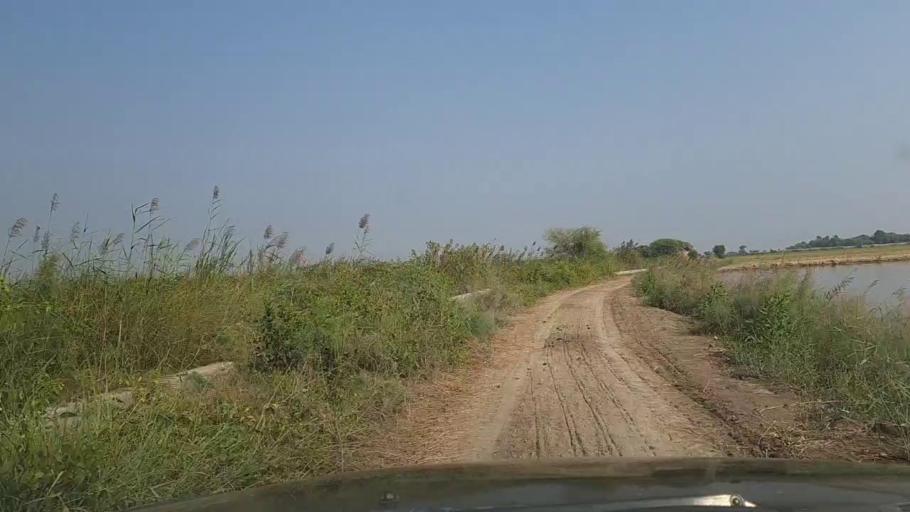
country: PK
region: Sindh
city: Mirpur Batoro
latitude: 24.6965
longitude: 68.2516
